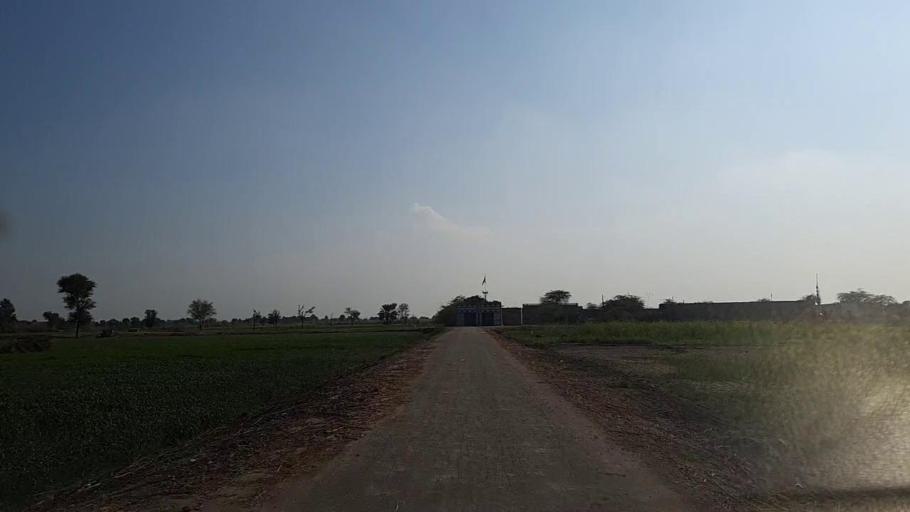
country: PK
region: Sindh
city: Jam Sahib
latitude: 26.2799
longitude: 68.6136
